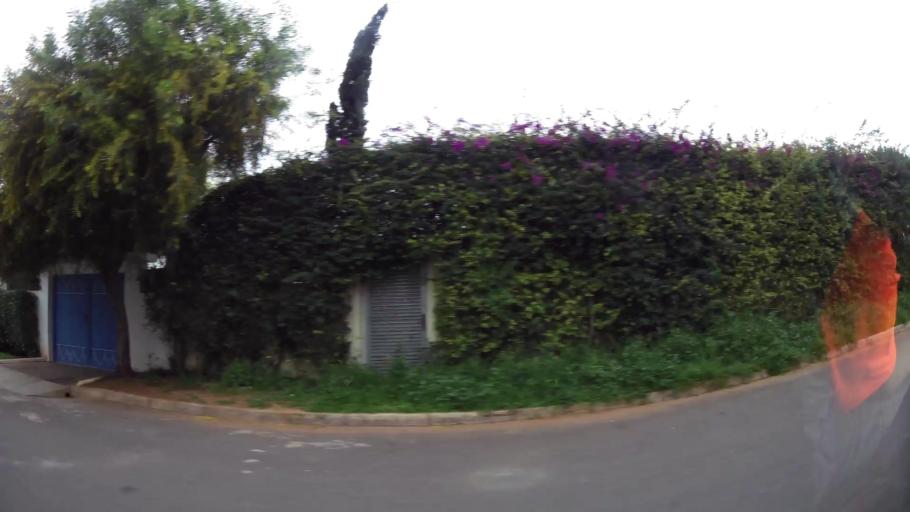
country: MA
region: Grand Casablanca
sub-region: Casablanca
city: Casablanca
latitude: 33.5439
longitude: -7.6361
